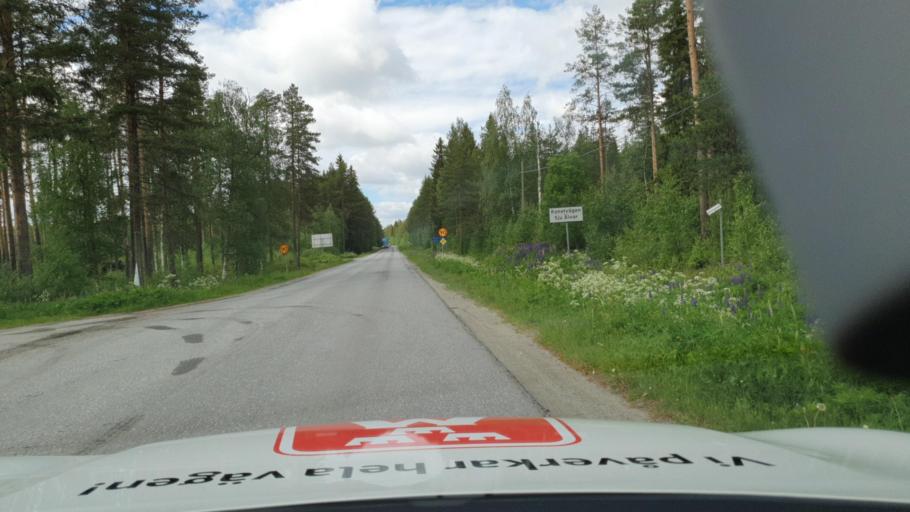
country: SE
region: Vaesterbotten
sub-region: Dorotea Kommun
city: Dorotea
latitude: 64.2599
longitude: 16.3755
